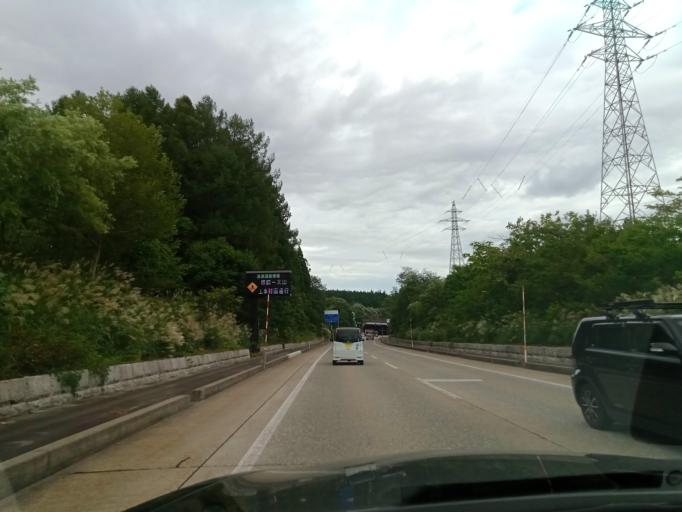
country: JP
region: Niigata
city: Arai
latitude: 36.8661
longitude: 138.1964
